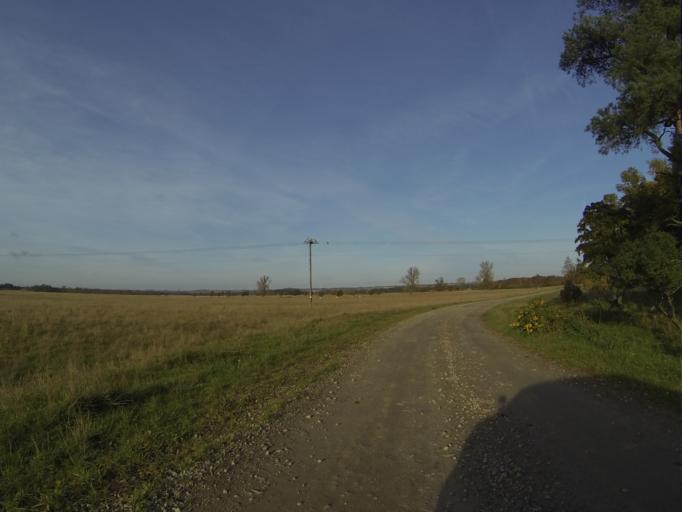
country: SE
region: Skane
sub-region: Lunds Kommun
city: Veberod
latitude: 55.7019
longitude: 13.4199
